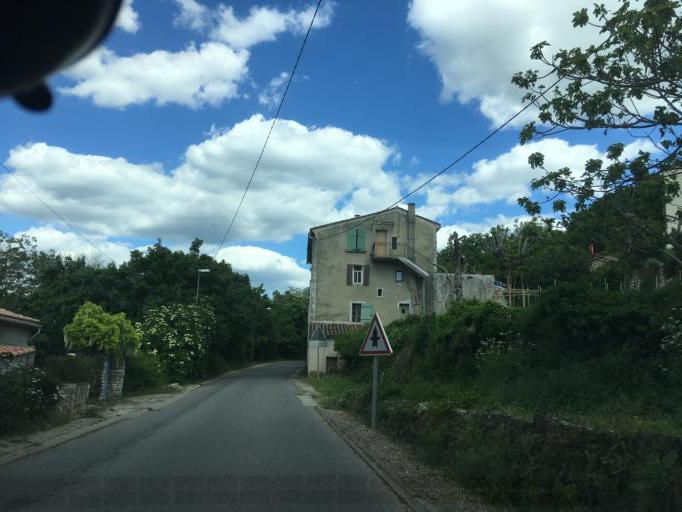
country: FR
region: Provence-Alpes-Cote d'Azur
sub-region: Departement du Var
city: Ginasservis
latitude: 43.5928
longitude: 5.8485
